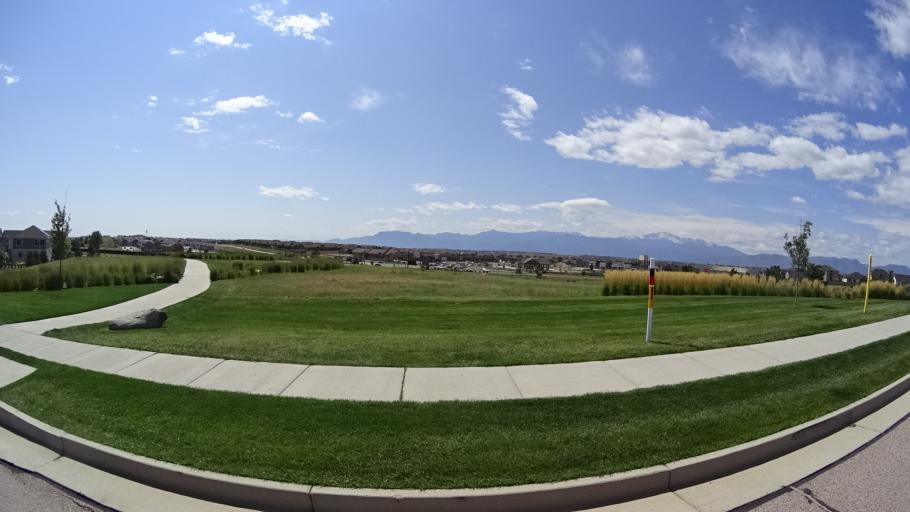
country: US
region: Colorado
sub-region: El Paso County
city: Cimarron Hills
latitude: 38.9287
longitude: -104.6805
